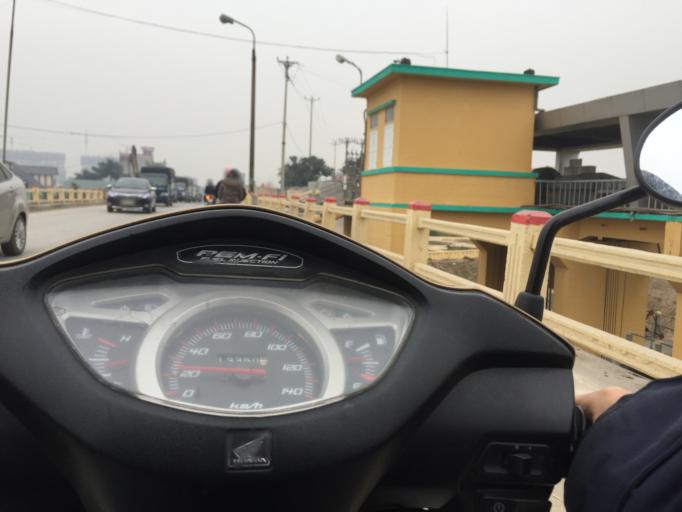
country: VN
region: Hung Yen
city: Van Giang
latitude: 20.9720
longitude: 105.9198
